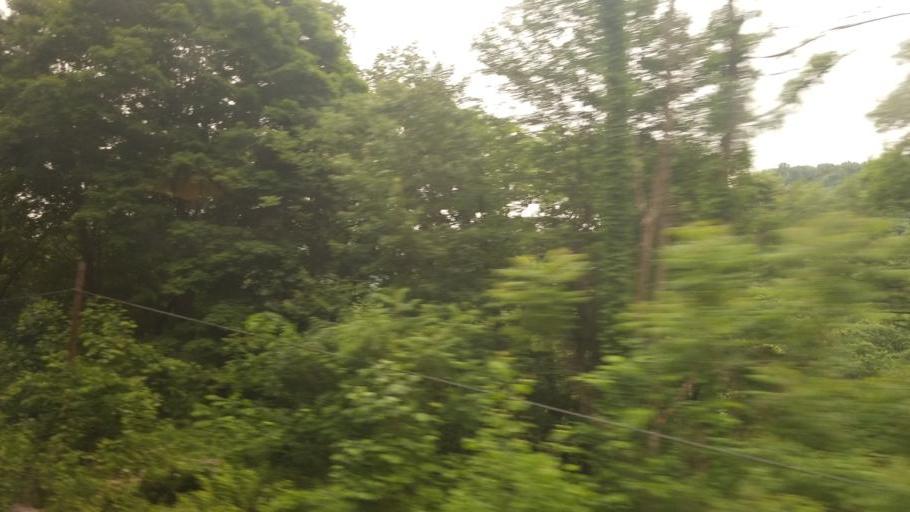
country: US
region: Pennsylvania
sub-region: Somerset County
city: Milford
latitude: 39.8345
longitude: -79.2668
